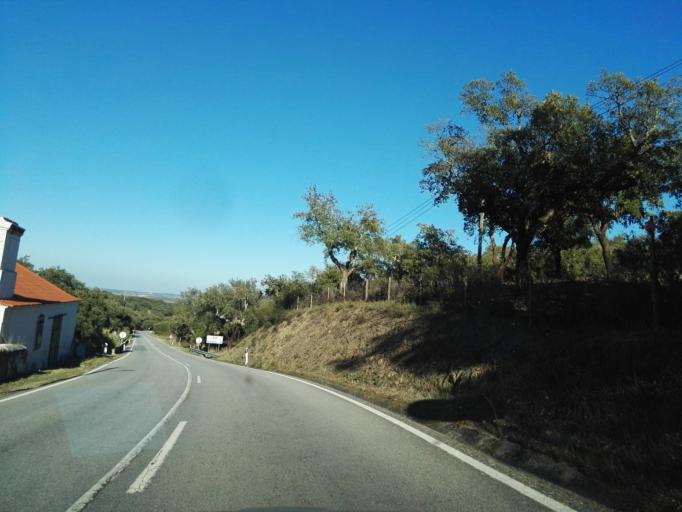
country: PT
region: Evora
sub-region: Estremoz
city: Estremoz
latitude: 38.7666
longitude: -7.7117
